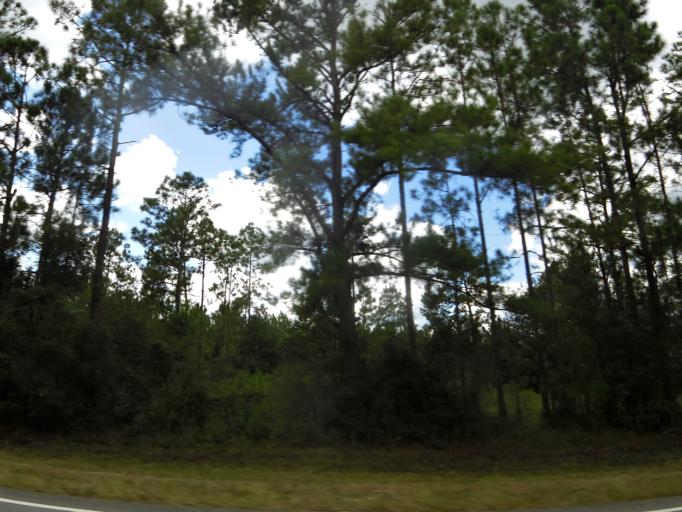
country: US
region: Georgia
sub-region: Charlton County
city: Folkston
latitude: 30.8911
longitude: -82.0158
